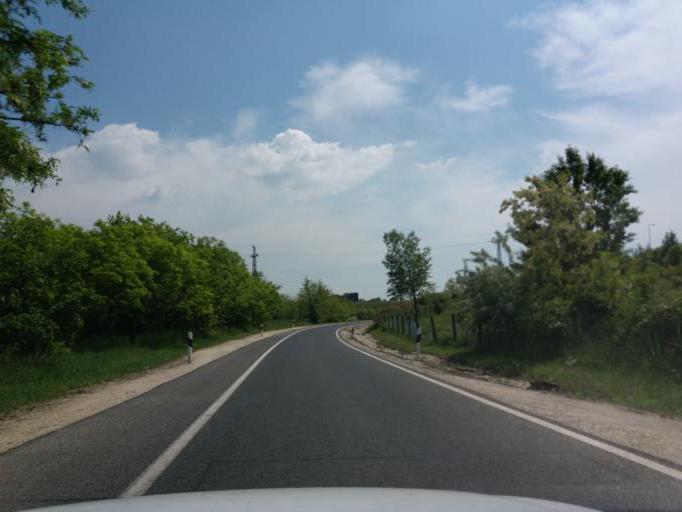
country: HU
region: Pest
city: Toeroekbalint
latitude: 47.4444
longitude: 18.8889
